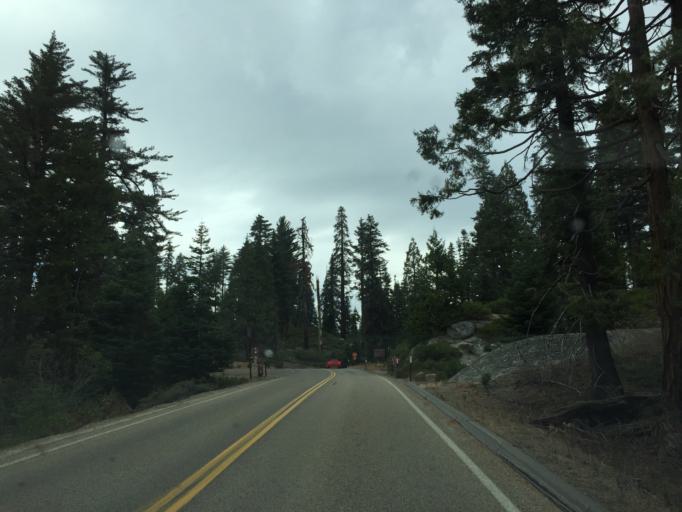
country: US
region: California
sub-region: Tulare County
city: Three Rivers
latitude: 36.7233
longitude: -118.9548
